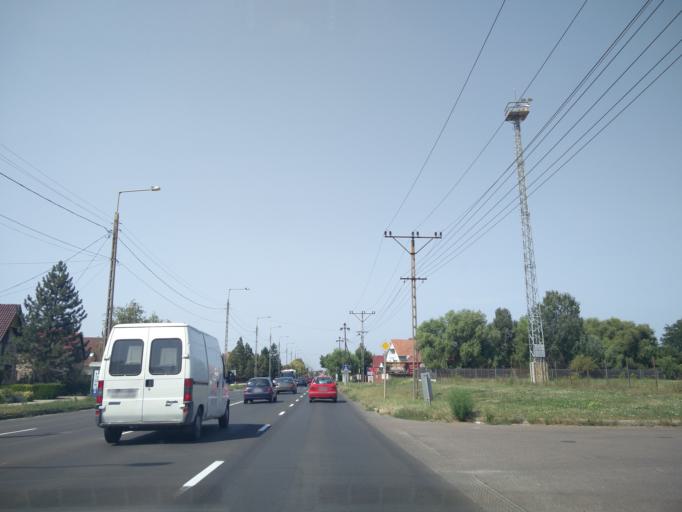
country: HU
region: Csongrad
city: Szeged
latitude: 46.2701
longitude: 20.0907
